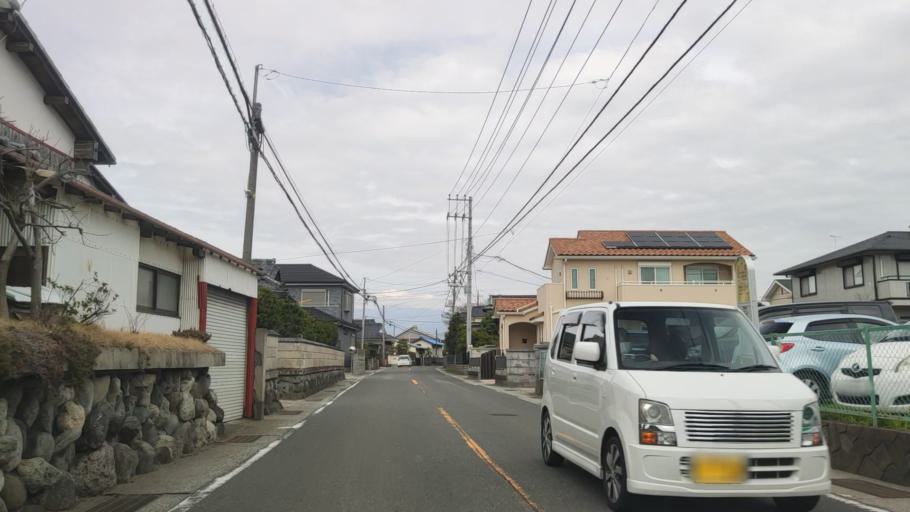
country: JP
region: Kanagawa
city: Ninomiya
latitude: 35.2948
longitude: 139.2332
